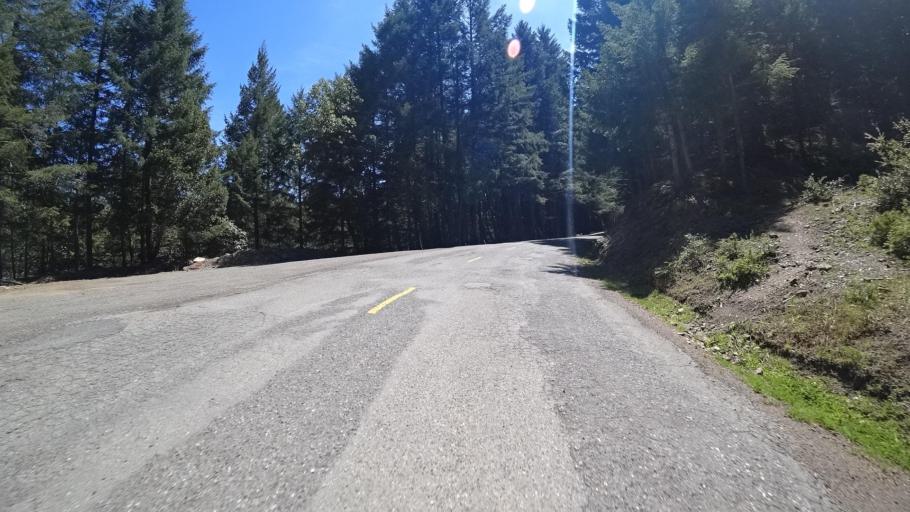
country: US
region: California
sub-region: Humboldt County
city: Rio Dell
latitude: 40.3080
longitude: -124.0619
